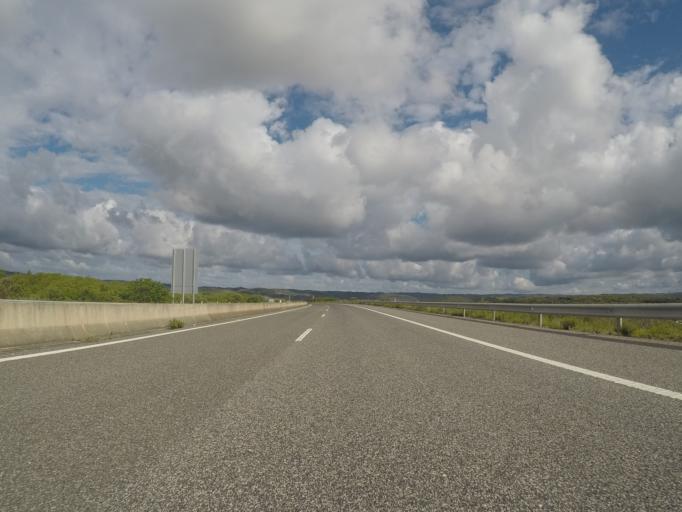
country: PT
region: Faro
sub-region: Lagos
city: Lagos
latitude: 37.1463
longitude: -8.7294
